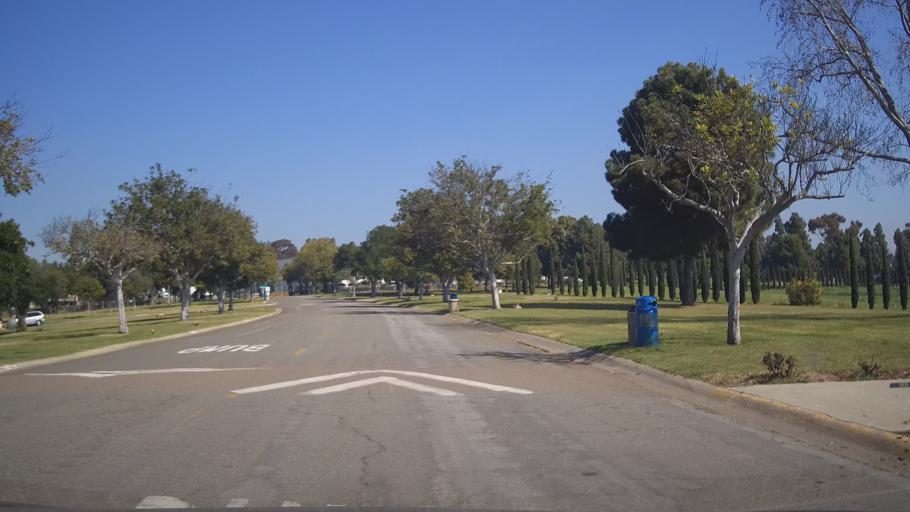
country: US
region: California
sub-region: San Diego County
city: National City
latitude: 32.7097
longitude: -117.1127
